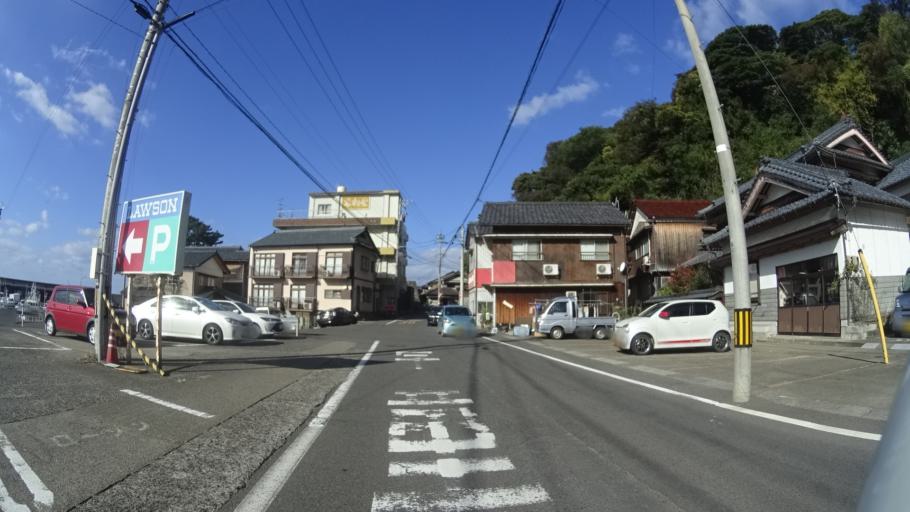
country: JP
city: Asahi
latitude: 35.9395
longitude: 135.9944
